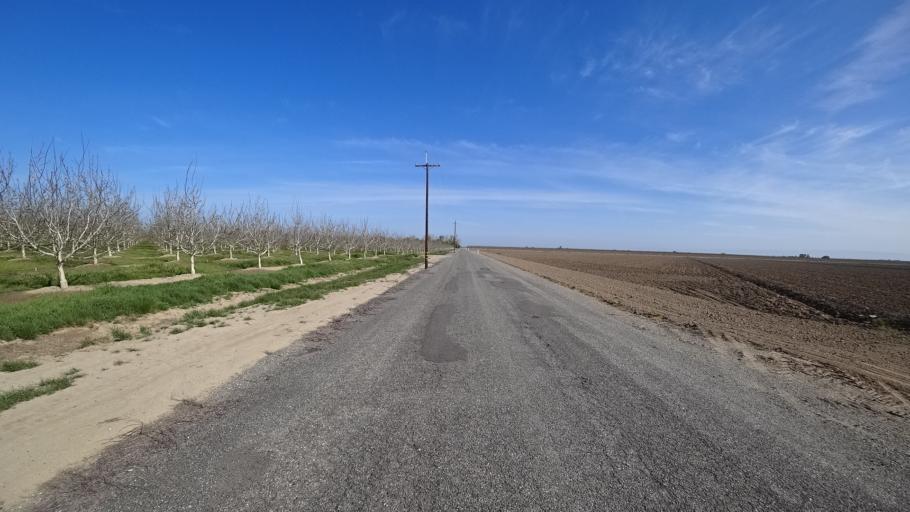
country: US
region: California
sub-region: Glenn County
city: Willows
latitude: 39.6135
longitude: -122.1170
